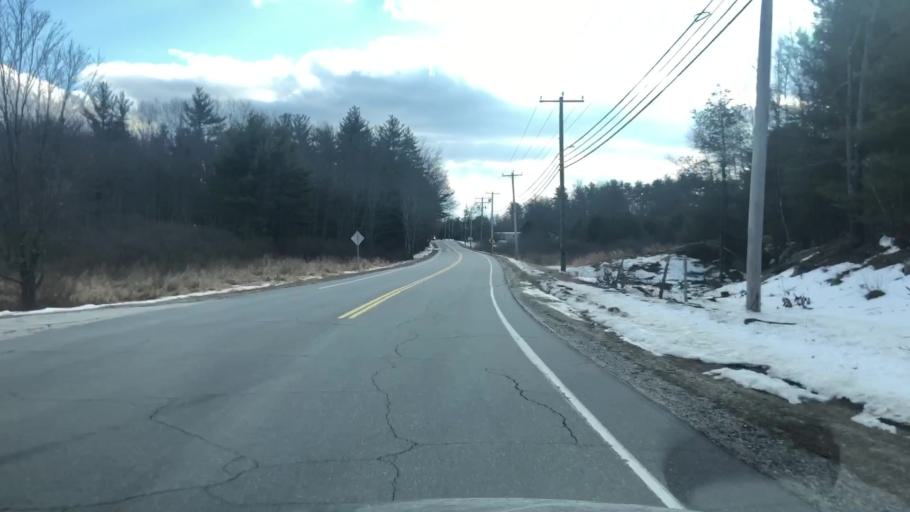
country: US
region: New Hampshire
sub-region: Hillsborough County
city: Milford
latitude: 42.8535
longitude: -71.6633
